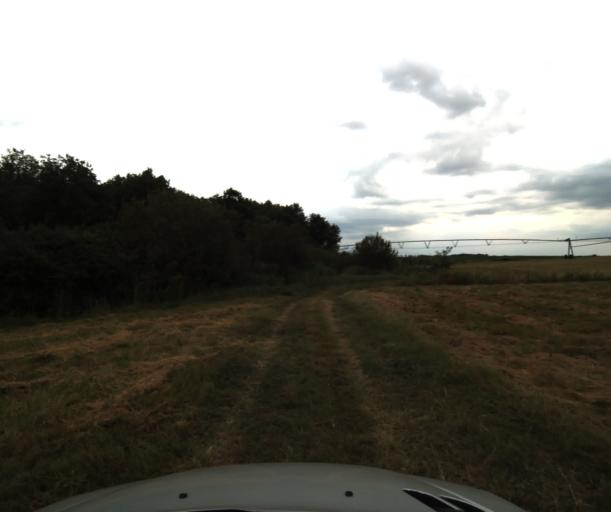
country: FR
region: Midi-Pyrenees
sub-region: Departement de la Haute-Garonne
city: Lherm
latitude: 43.4592
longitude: 1.2042
